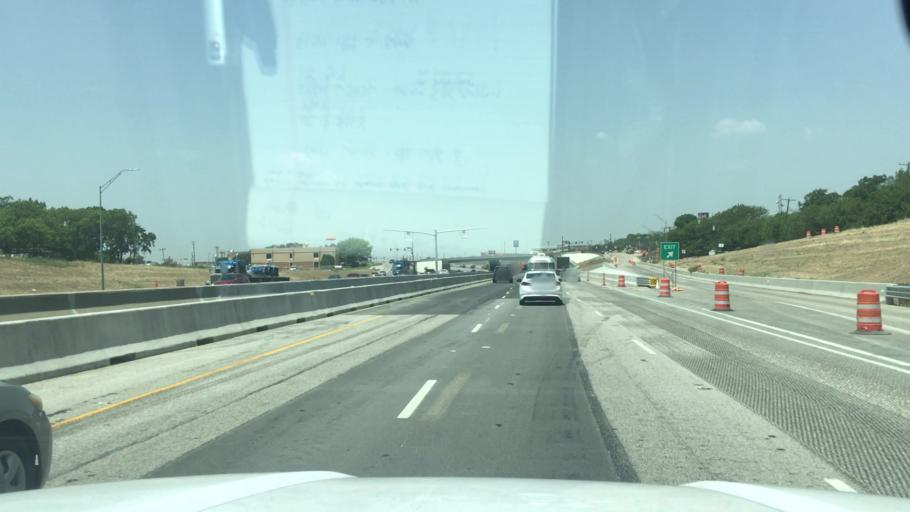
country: US
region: Texas
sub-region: Tarrant County
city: Euless
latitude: 32.8383
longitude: -97.0778
